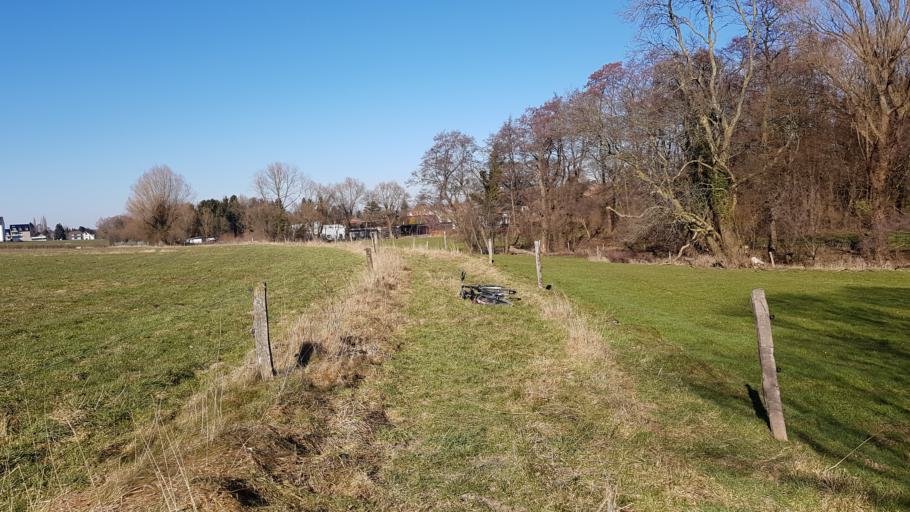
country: DE
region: North Rhine-Westphalia
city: Stolberg
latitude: 50.7705
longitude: 6.1690
